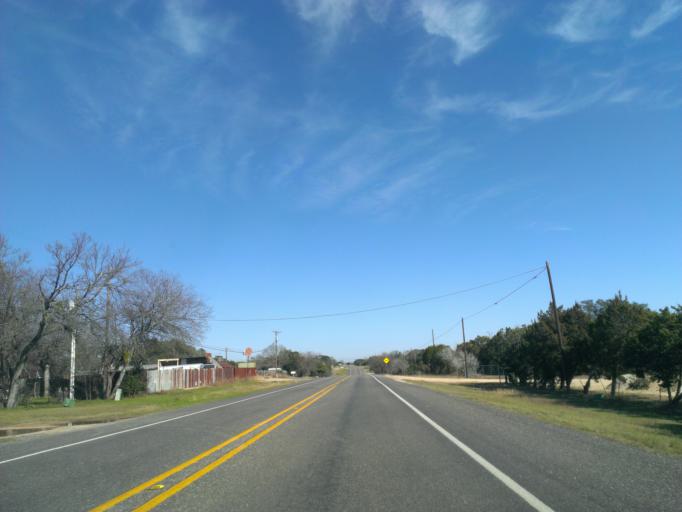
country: US
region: Texas
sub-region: Bell County
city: Belton
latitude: 31.0395
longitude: -97.5228
